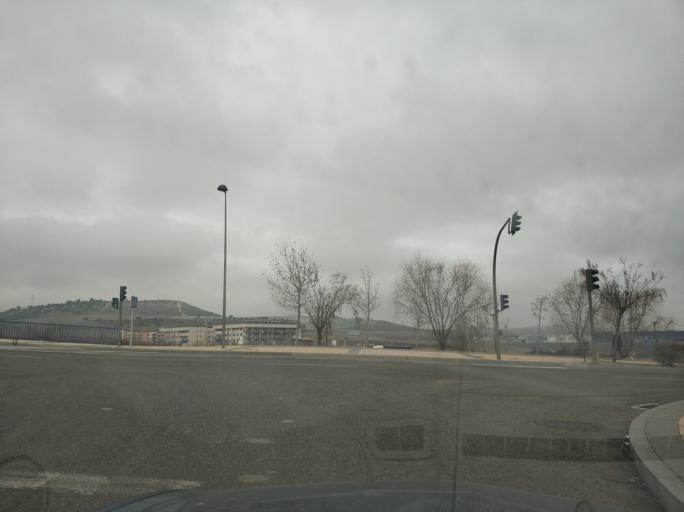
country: ES
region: Castille and Leon
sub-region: Provincia de Valladolid
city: Arroyo
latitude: 41.6205
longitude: -4.7887
